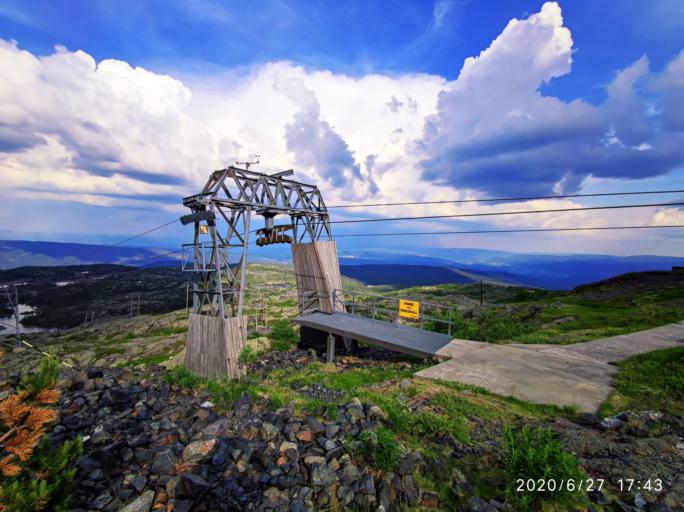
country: NO
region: Buskerud
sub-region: Kongsberg
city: Kongsberg
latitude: 59.6713
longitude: 9.5220
